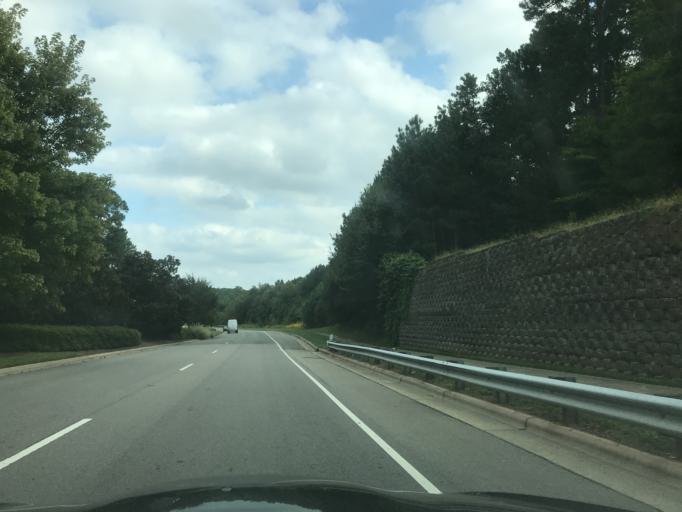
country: US
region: North Carolina
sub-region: Durham County
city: Durham
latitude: 35.9334
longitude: -78.8944
